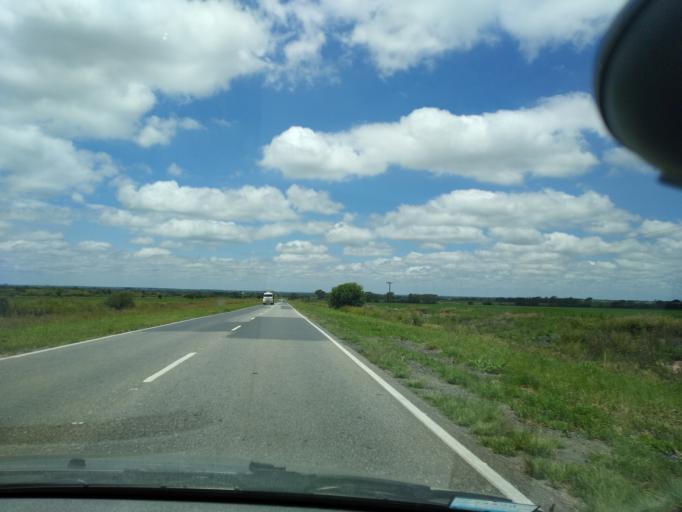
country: AR
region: Cordoba
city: Alta Gracia
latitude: -31.6521
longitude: -64.3010
